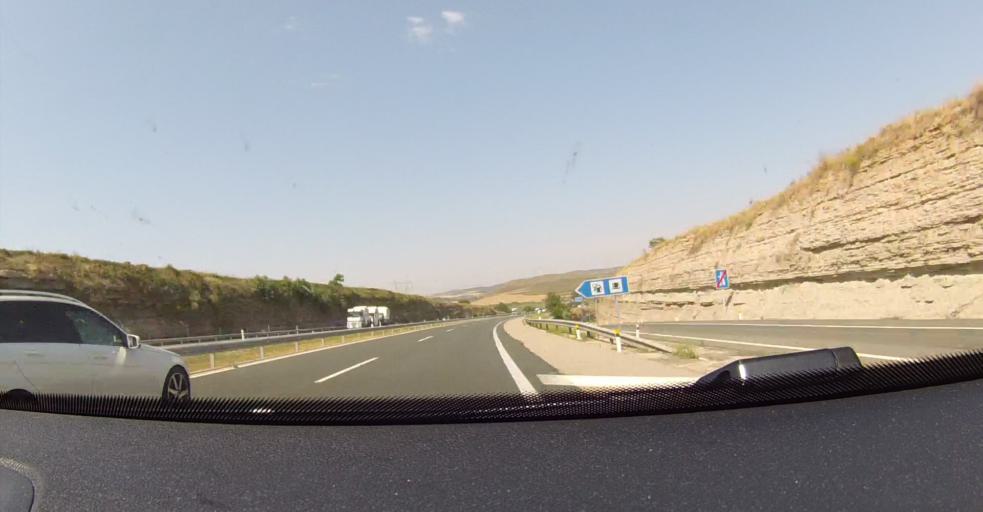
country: ES
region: Castille and Leon
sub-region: Provincia de Burgos
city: Briviesca
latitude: 42.5323
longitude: -3.3155
